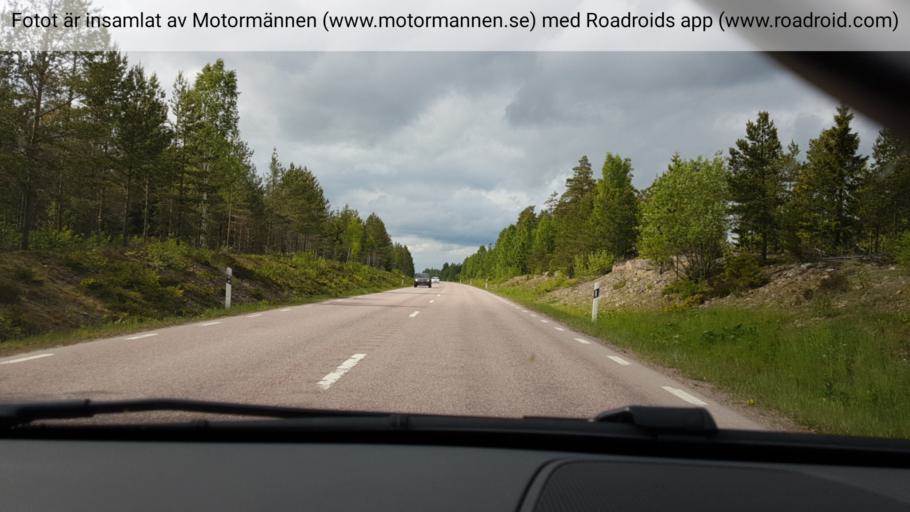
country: SE
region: Uppsala
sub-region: Tierps Kommun
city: Tierp
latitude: 60.2952
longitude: 17.5770
